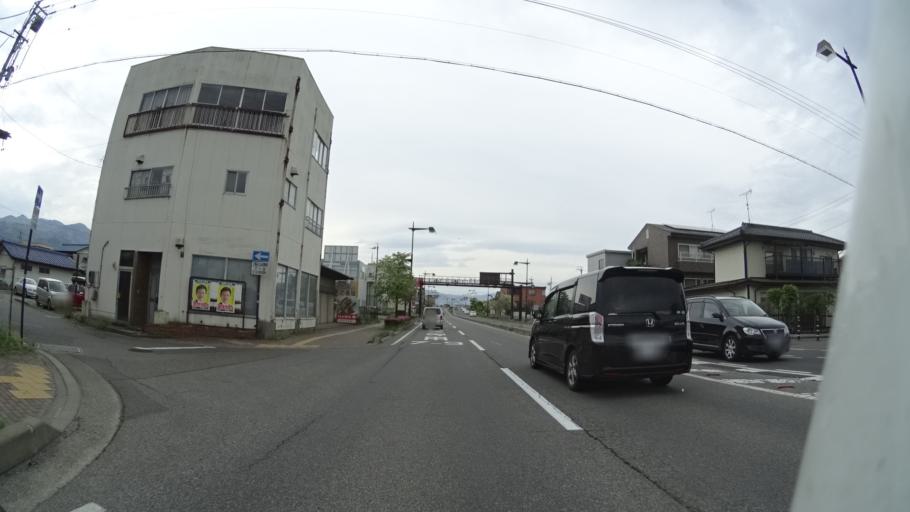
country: JP
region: Nagano
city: Nagano-shi
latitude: 36.6186
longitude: 138.1816
